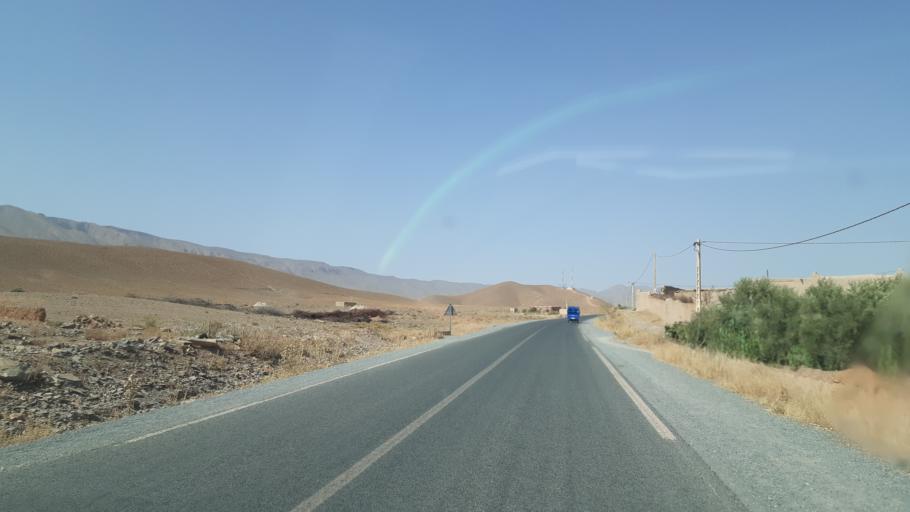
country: MA
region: Meknes-Tafilalet
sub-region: Errachidia
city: Errachidia
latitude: 32.2493
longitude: -4.5812
